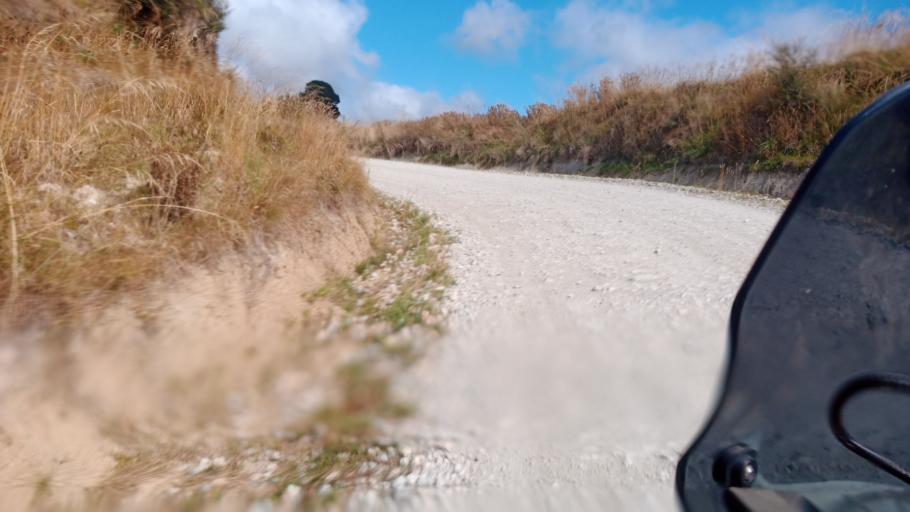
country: NZ
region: Hawke's Bay
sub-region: Wairoa District
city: Wairoa
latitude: -38.6032
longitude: 177.4763
